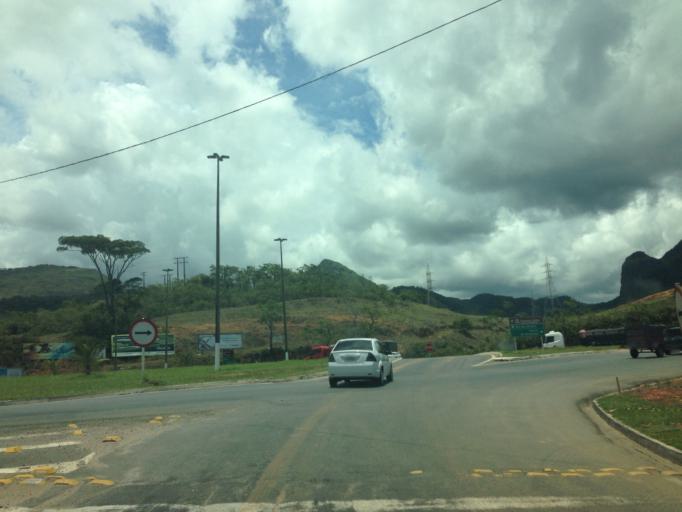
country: BR
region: Espirito Santo
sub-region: Guarapari
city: Guarapari
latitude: -20.6280
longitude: -40.5276
